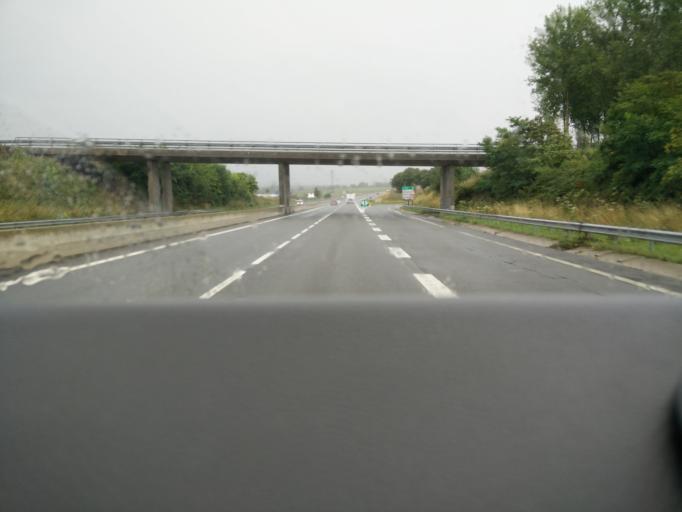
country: FR
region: Nord-Pas-de-Calais
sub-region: Departement du Pas-de-Calais
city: Hesdin
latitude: 50.3633
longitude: 2.0240
